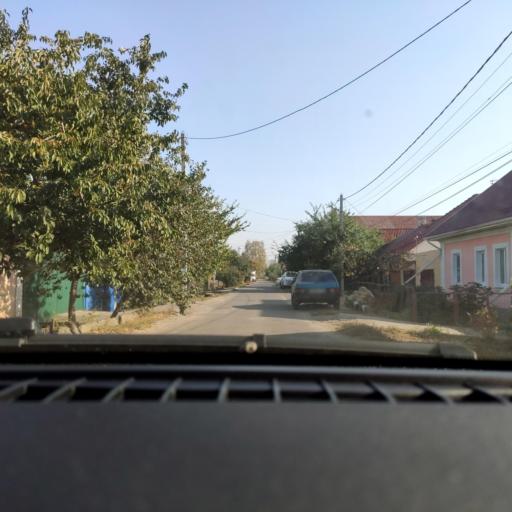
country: RU
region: Voronezj
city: Voronezh
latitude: 51.6724
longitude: 39.2651
